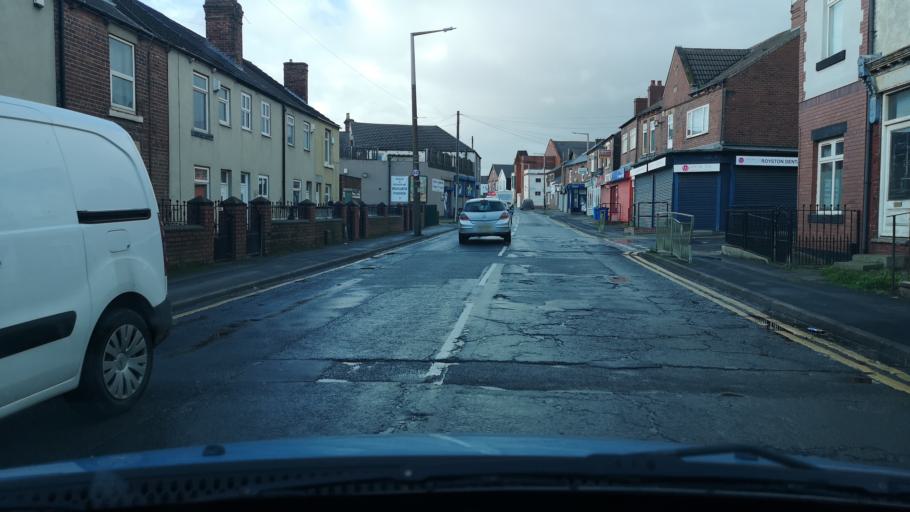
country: GB
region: England
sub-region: Barnsley
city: Royston
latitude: 53.6011
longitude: -1.4447
